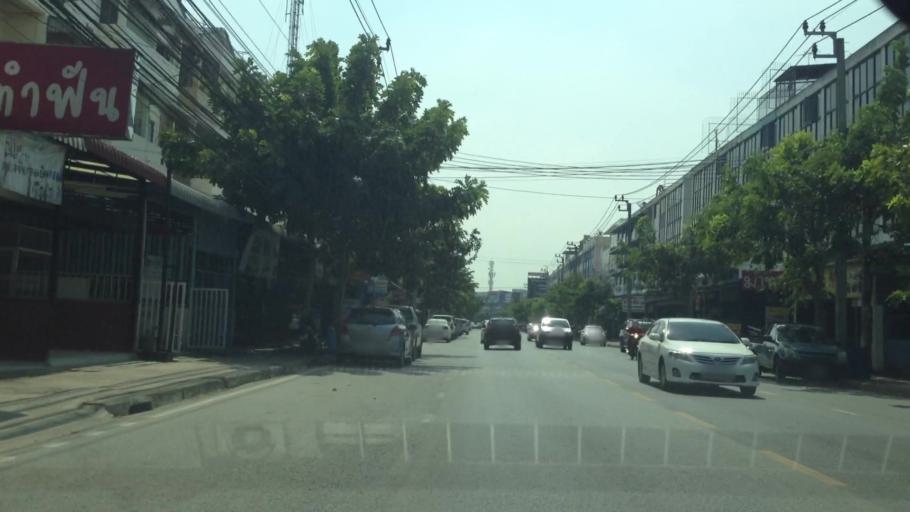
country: TH
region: Bangkok
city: Sai Mai
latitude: 13.8986
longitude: 100.6380
